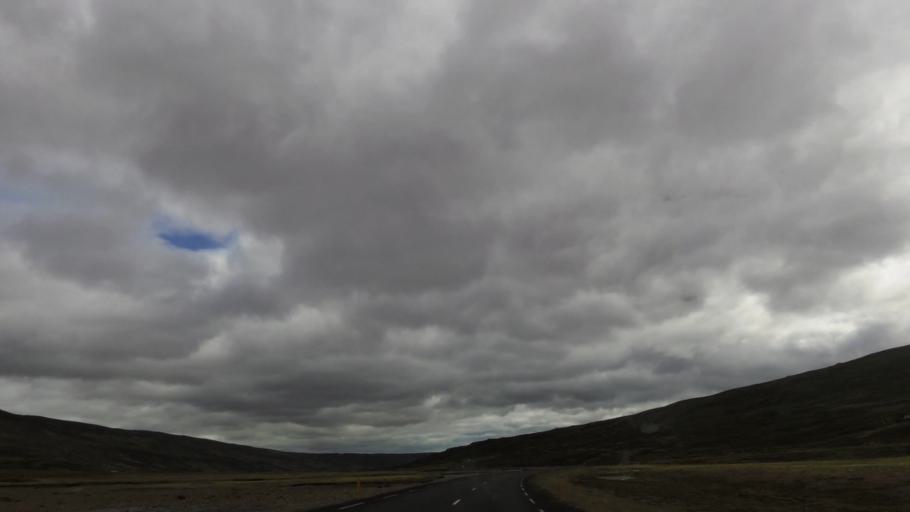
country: IS
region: West
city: Stykkisholmur
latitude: 65.7583
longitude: -21.8731
